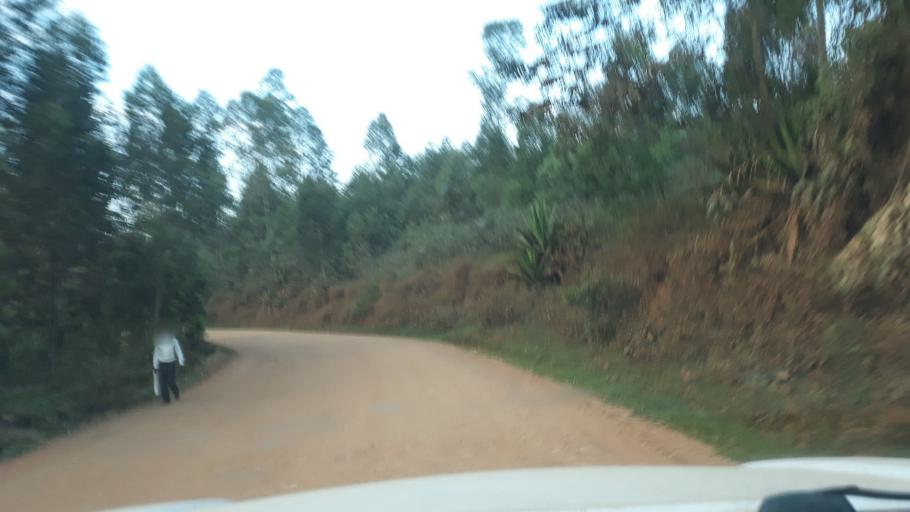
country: CD
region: South Kivu
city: Bukavu
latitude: -2.6241
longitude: 28.8767
